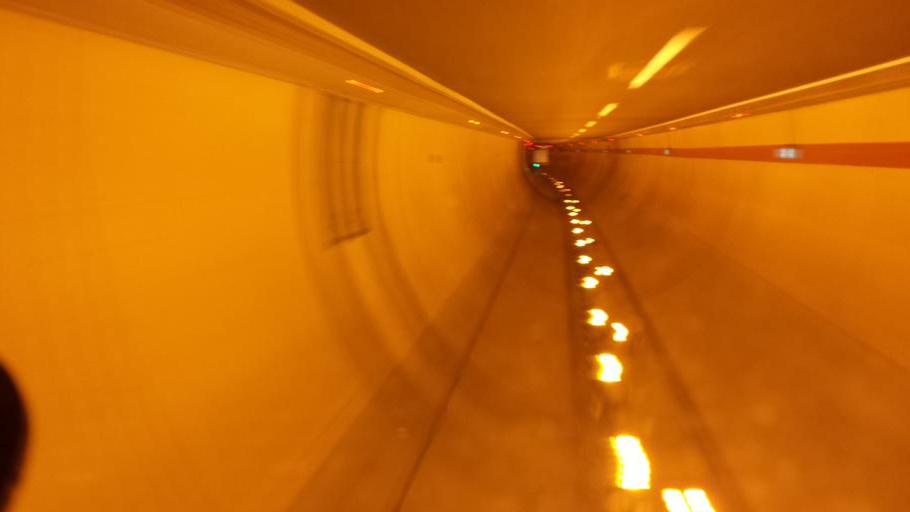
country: HR
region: Primorsko-Goranska
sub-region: Grad Delnice
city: Delnice
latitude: 45.3646
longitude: 14.7693
